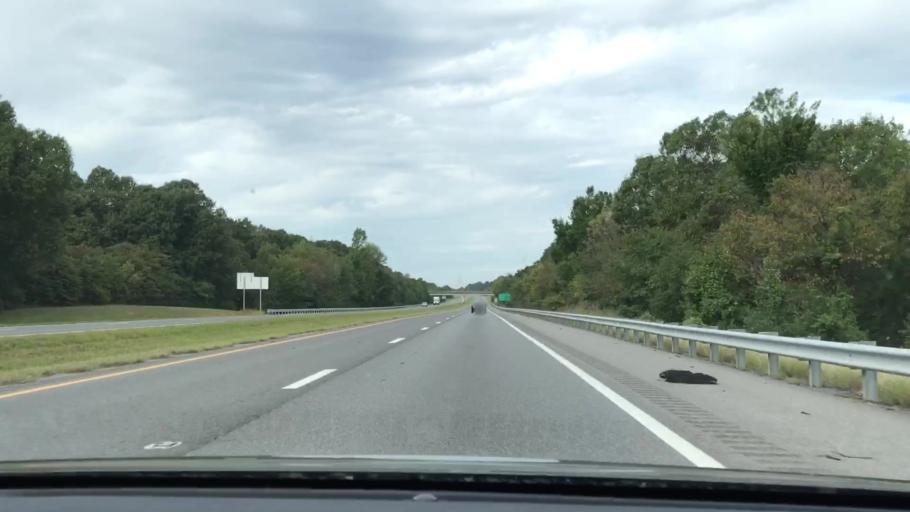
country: US
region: Kentucky
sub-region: Marshall County
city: Benton
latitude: 36.8478
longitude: -88.3870
